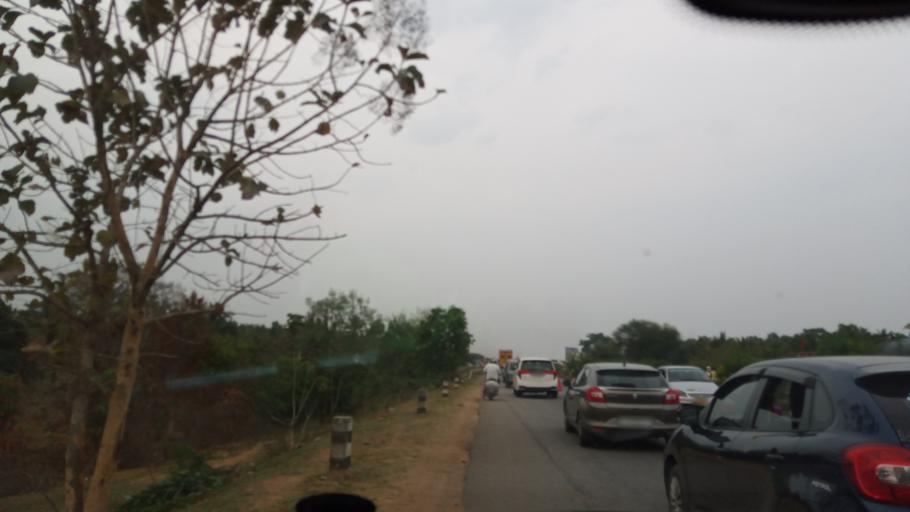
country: IN
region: Karnataka
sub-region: Ramanagara
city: Magadi
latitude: 13.0547
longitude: 77.1549
